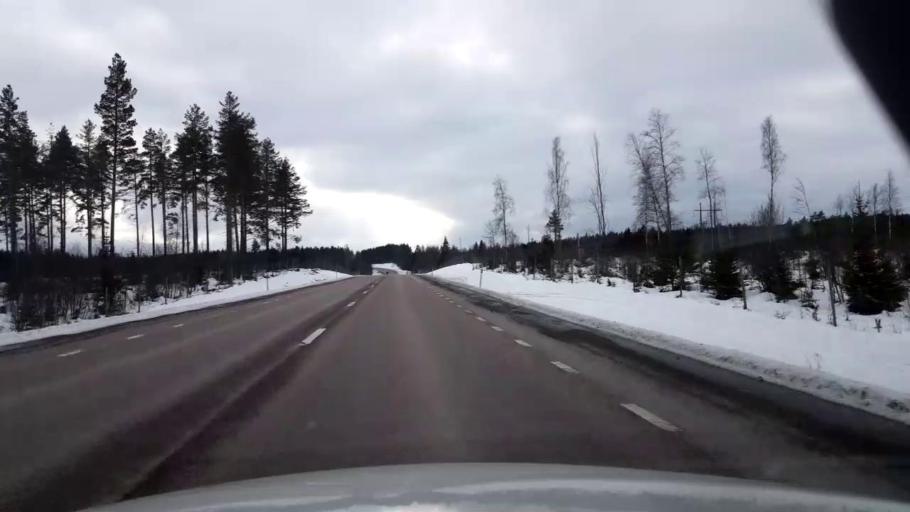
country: SE
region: Gaevleborg
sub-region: Nordanstigs Kommun
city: Bergsjoe
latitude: 61.9955
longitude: 17.2416
